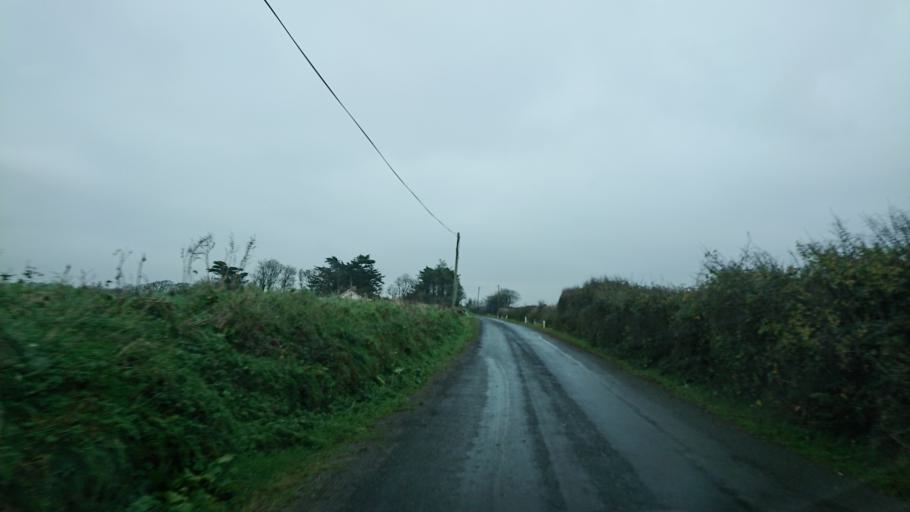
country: IE
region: Munster
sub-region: Waterford
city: Dunmore East
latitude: 52.1679
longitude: -7.0225
